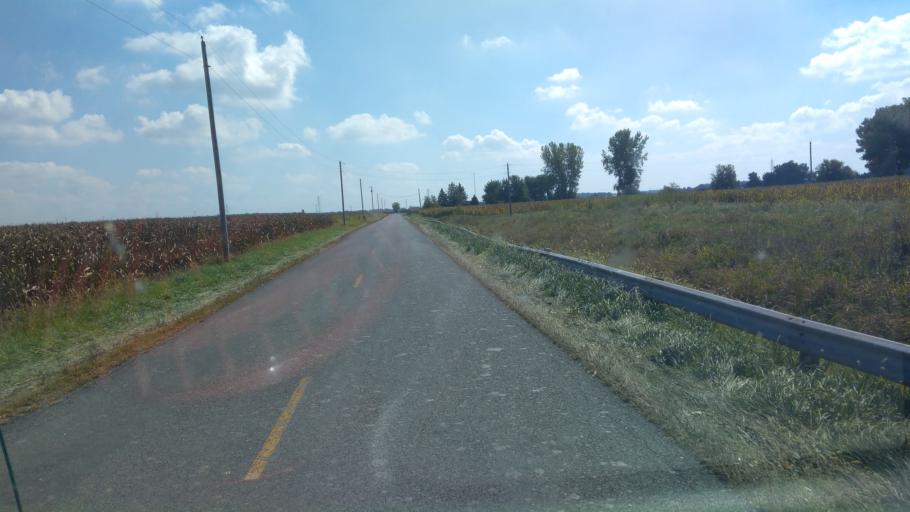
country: US
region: Ohio
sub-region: Hardin County
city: Ada
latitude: 40.6795
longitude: -83.8421
